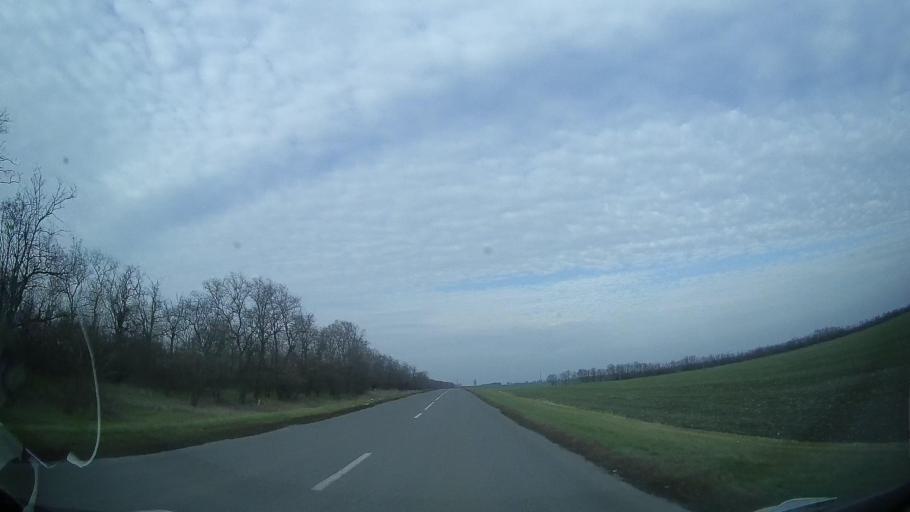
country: RU
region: Rostov
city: Zernograd
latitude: 46.9212
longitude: 40.3389
